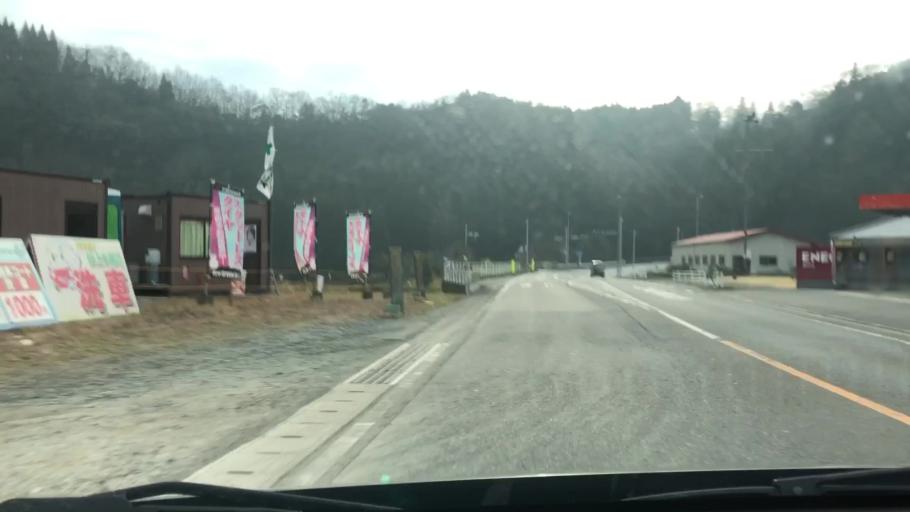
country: JP
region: Oita
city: Takedamachi
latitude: 32.9823
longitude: 131.5476
